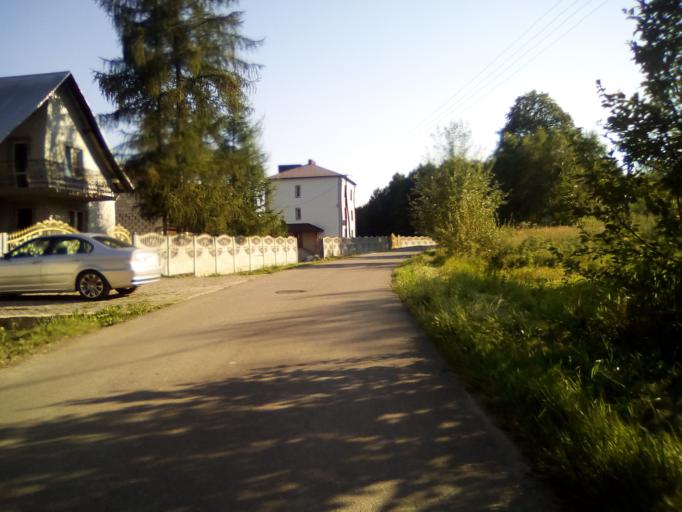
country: PL
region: Subcarpathian Voivodeship
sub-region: Powiat brzozowski
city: Domaradz
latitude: 49.8087
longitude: 21.9442
